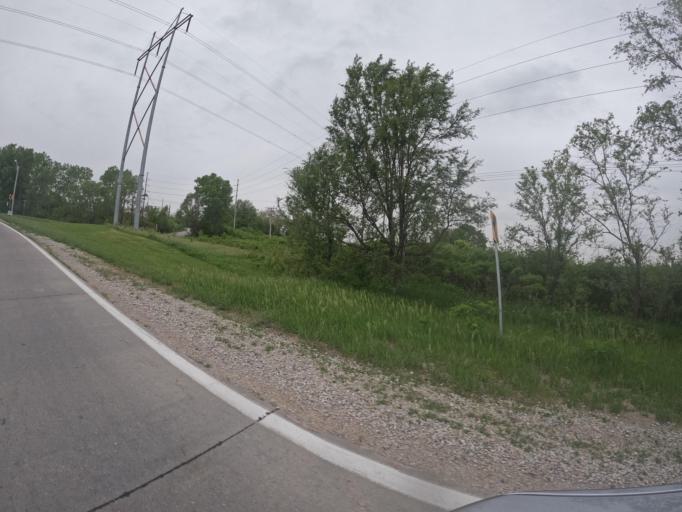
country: US
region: Nebraska
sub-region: Cass County
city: Plattsmouth
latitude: 41.0455
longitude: -95.9578
